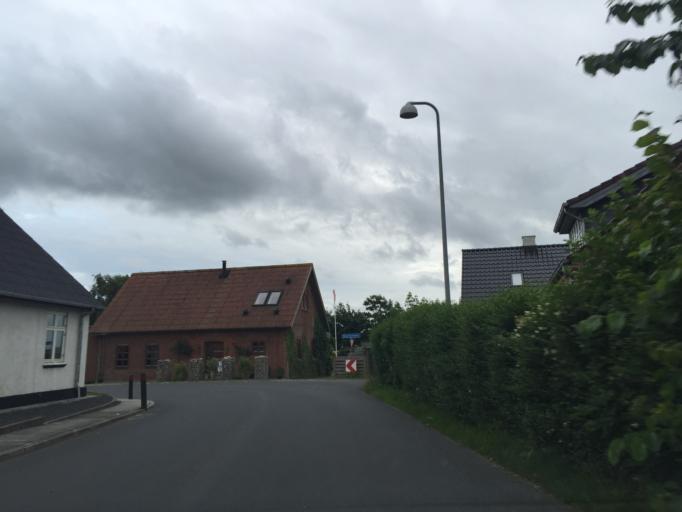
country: DK
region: Central Jutland
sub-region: Silkeborg Kommune
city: Silkeborg
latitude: 56.2253
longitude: 9.5623
